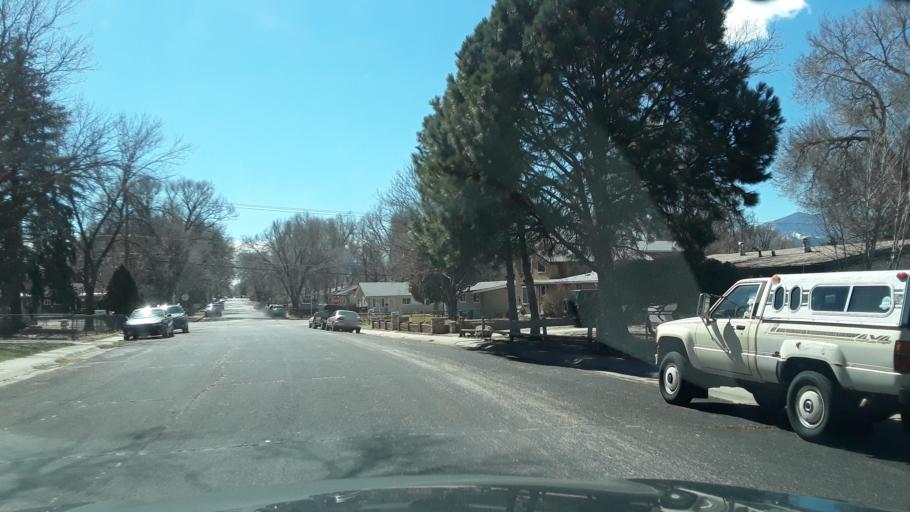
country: US
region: Colorado
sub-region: El Paso County
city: Colorado Springs
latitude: 38.8795
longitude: -104.8045
